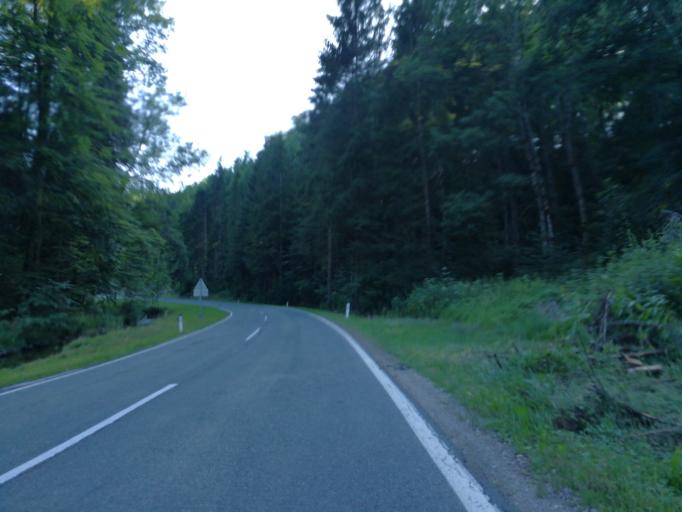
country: AT
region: Salzburg
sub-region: Politischer Bezirk Salzburg-Umgebung
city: Koppl
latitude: 47.8280
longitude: 13.1516
